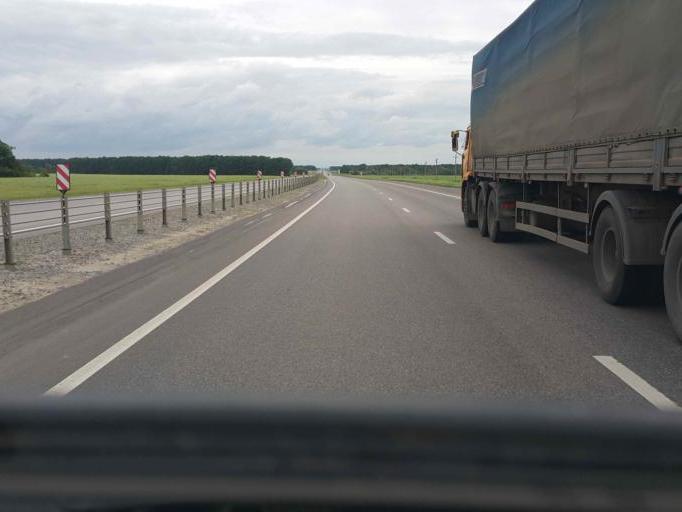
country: RU
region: Tambov
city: Zavoronezhskoye
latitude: 52.9058
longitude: 40.6429
